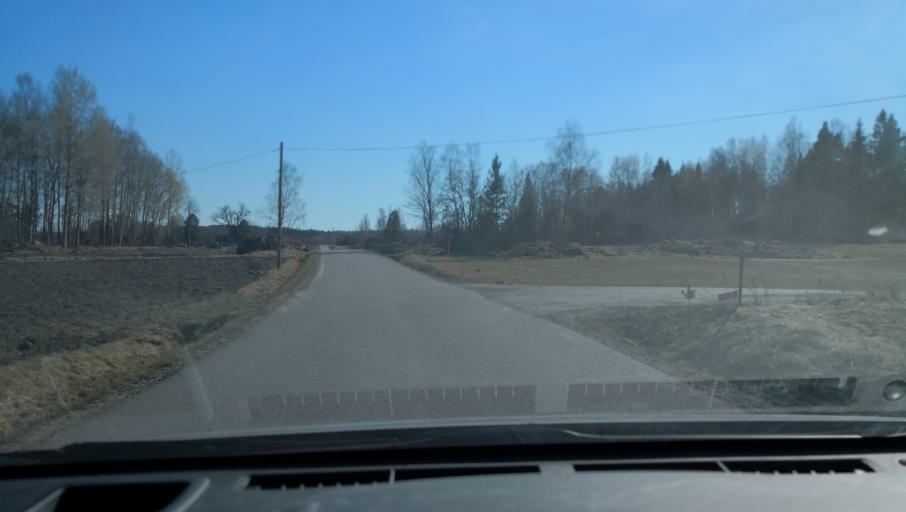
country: SE
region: Vaestmanland
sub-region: Sala Kommun
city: Sala
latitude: 60.0824
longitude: 16.4975
